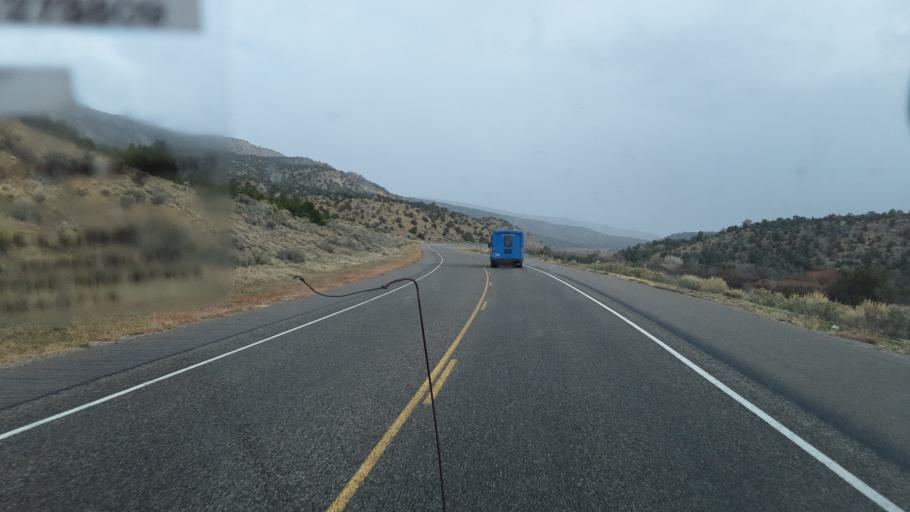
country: US
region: New Mexico
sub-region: Rio Arriba County
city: Santa Teresa
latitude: 36.3687
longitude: -106.5056
